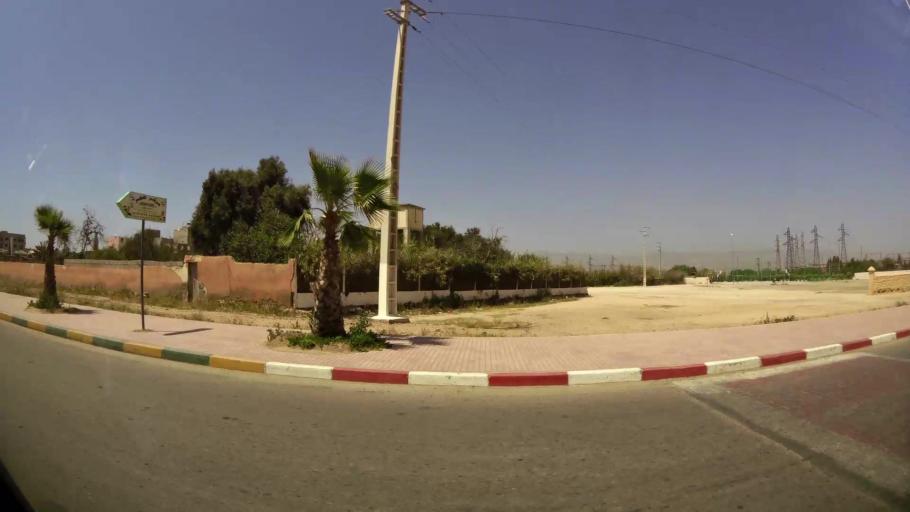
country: MA
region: Souss-Massa-Draa
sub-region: Inezgane-Ait Mellou
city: Inezgane
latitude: 30.3528
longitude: -9.4897
